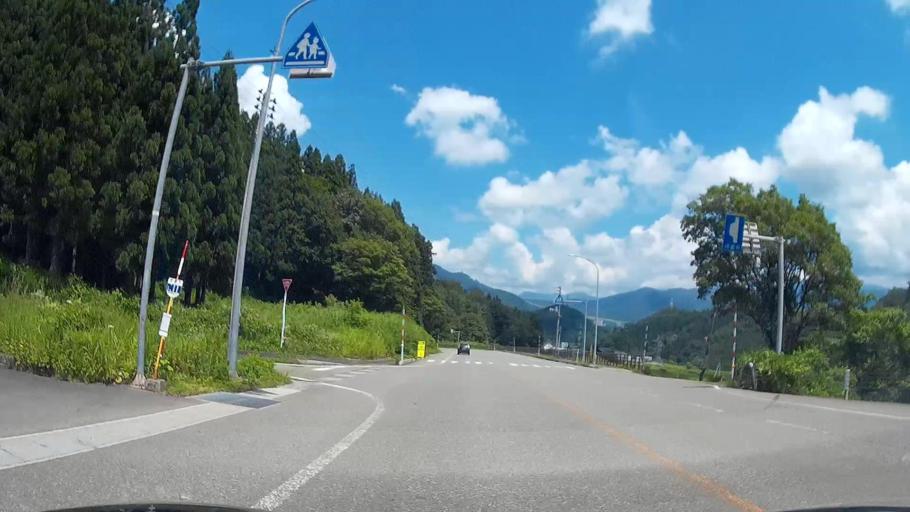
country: JP
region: Niigata
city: Shiozawa
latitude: 36.9139
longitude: 138.8019
